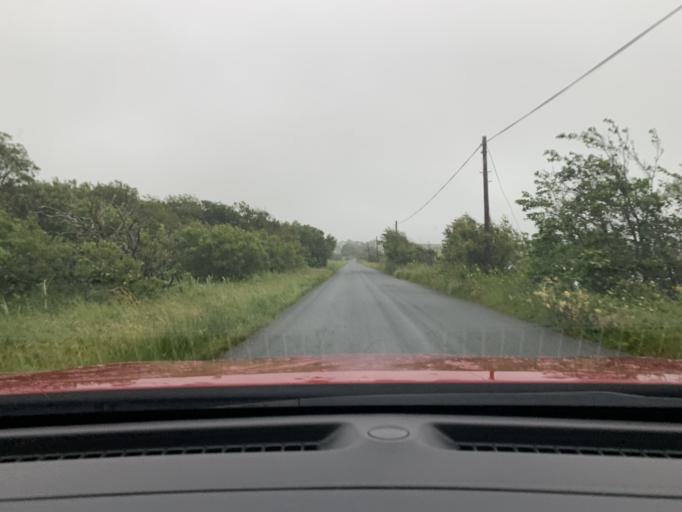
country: IE
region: Connaught
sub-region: County Leitrim
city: Kinlough
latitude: 54.4471
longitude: -8.4448
